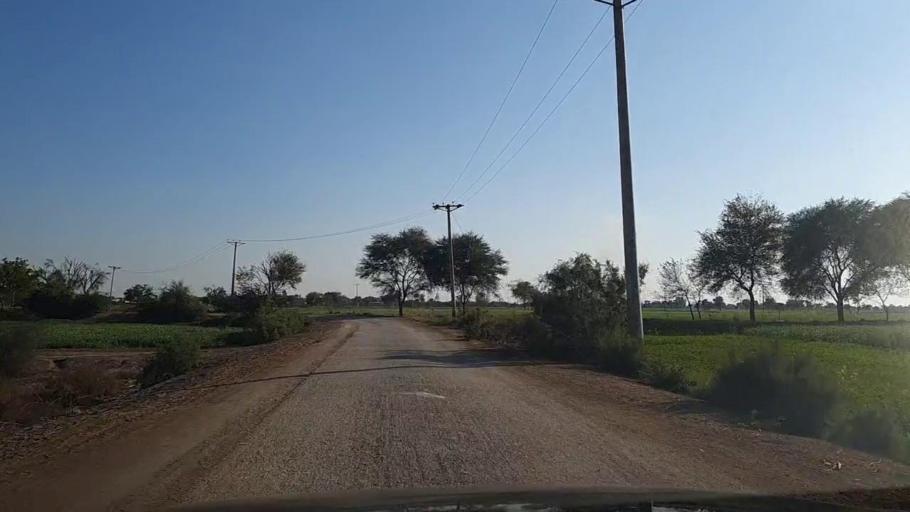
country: PK
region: Sindh
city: Nawabshah
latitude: 26.2097
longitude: 68.3741
